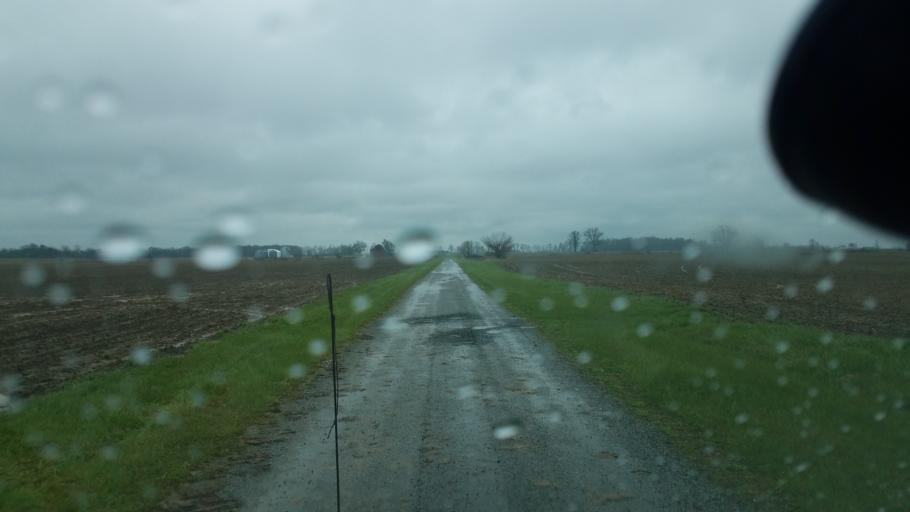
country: US
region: Ohio
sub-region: Union County
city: Richwood
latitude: 40.5211
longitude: -83.3608
